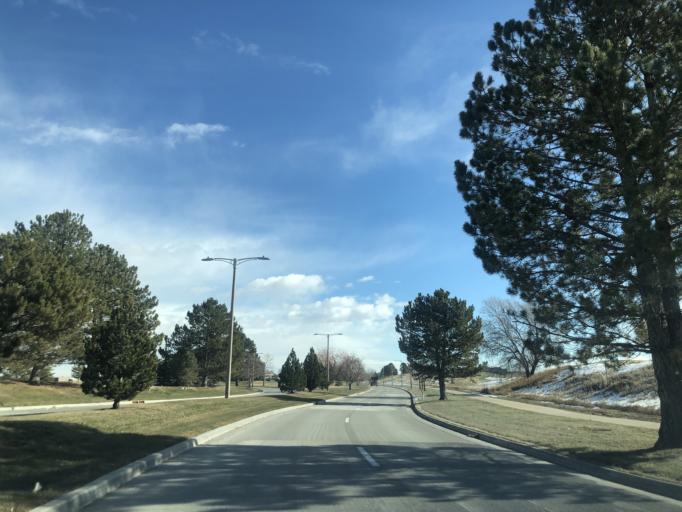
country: US
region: Colorado
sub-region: Douglas County
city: Meridian
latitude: 39.5487
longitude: -104.8521
